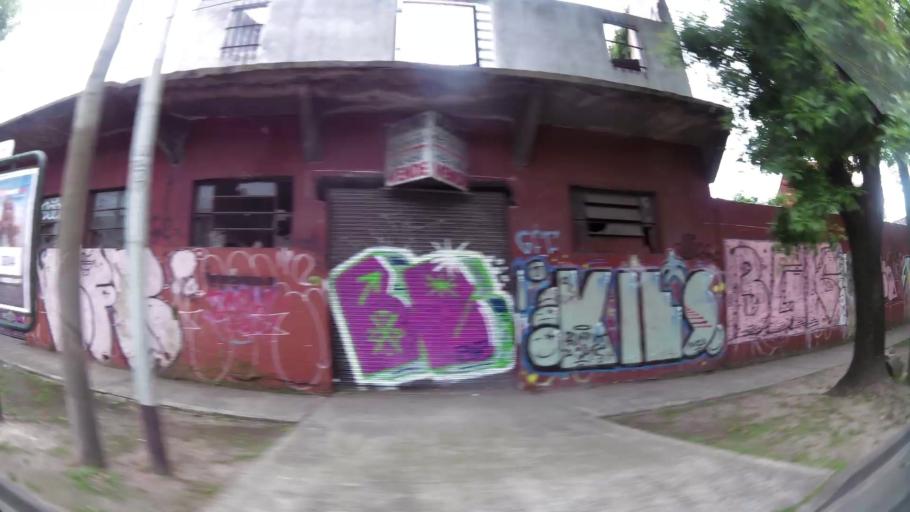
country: AR
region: Buenos Aires
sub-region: Partido de Avellaneda
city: Avellaneda
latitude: -34.6759
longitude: -58.3537
